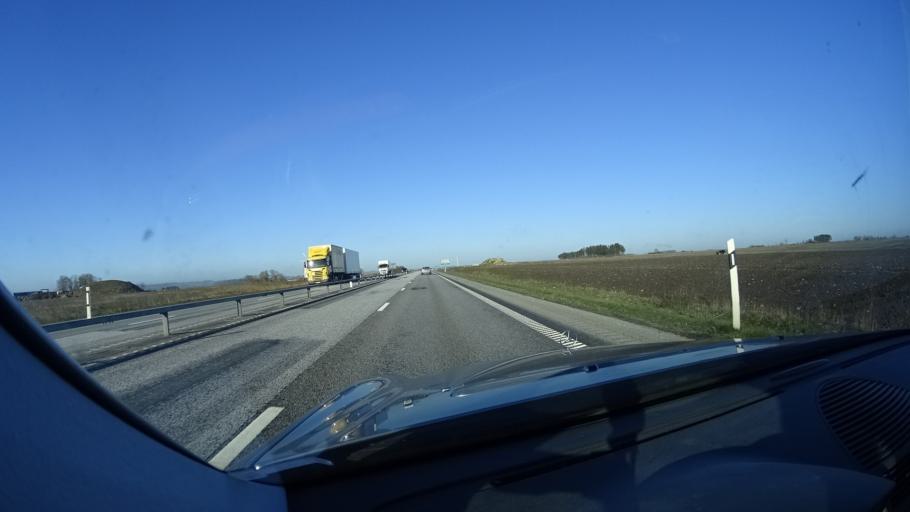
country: SE
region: Skane
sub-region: Eslovs Kommun
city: Eslov
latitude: 55.7750
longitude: 13.3534
